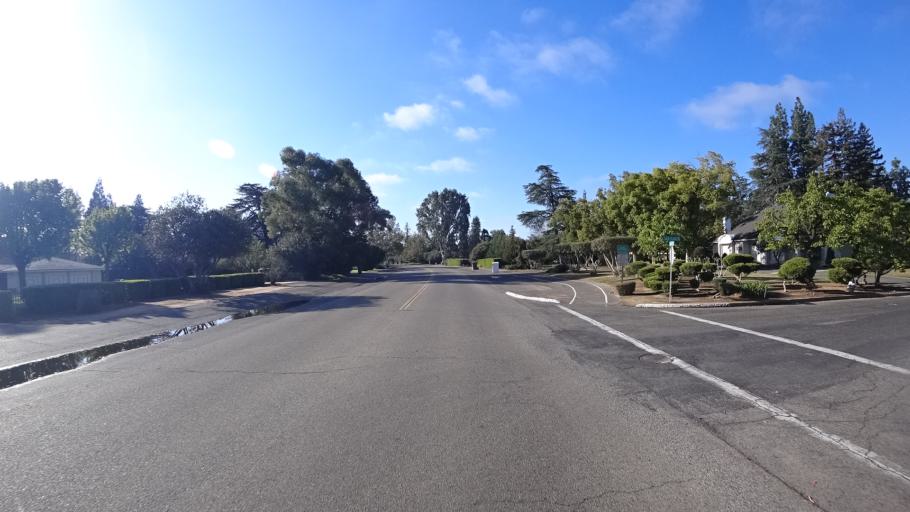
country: US
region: California
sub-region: Fresno County
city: Fresno
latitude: 36.8133
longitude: -119.8354
